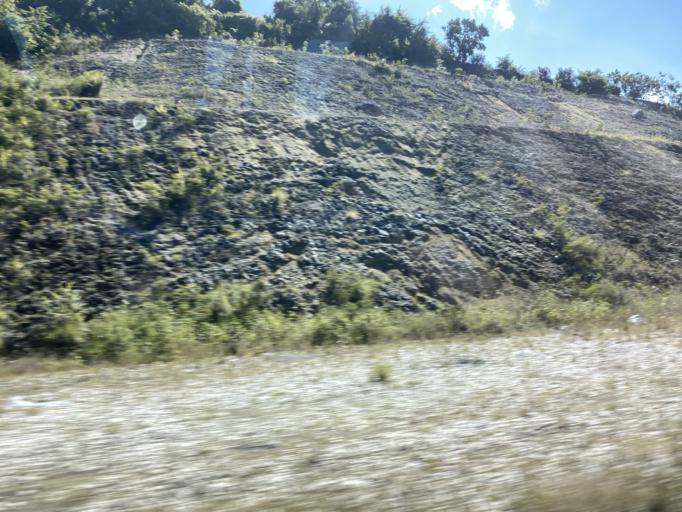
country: DO
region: Puerto Plata
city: Imbert
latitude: 19.8252
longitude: -70.7744
